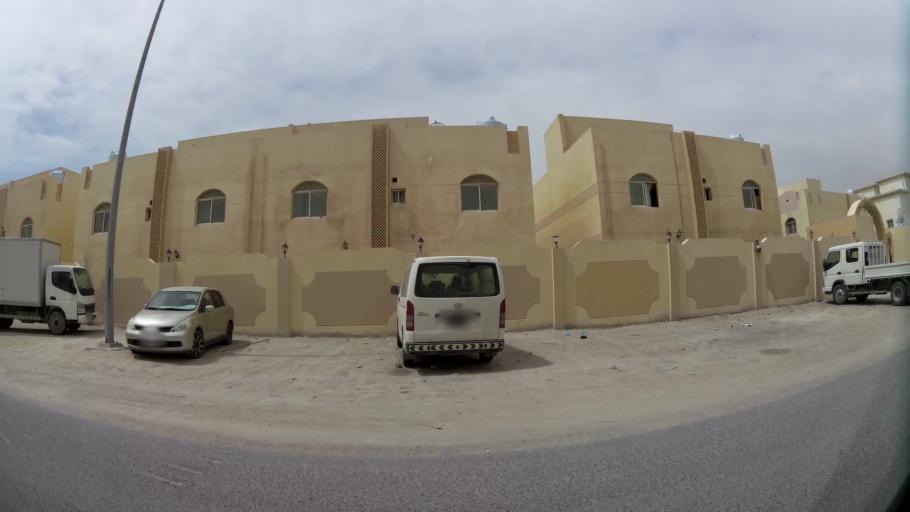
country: QA
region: Baladiyat ar Rayyan
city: Ar Rayyan
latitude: 25.2217
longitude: 51.4615
